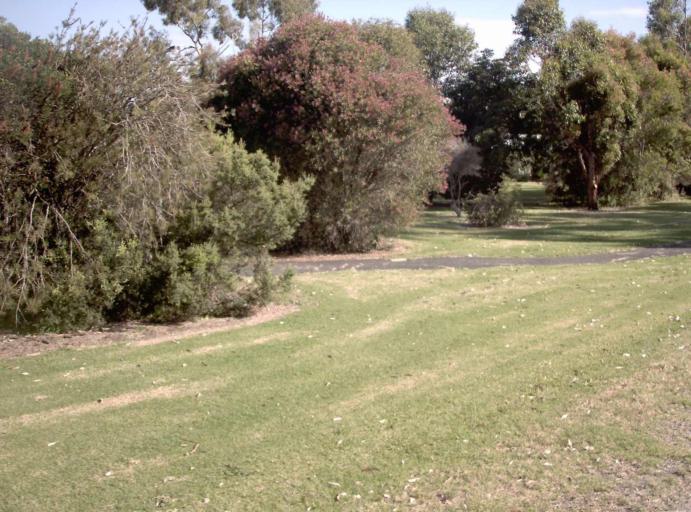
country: AU
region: Victoria
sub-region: East Gippsland
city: Lakes Entrance
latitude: -37.7893
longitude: 148.5362
